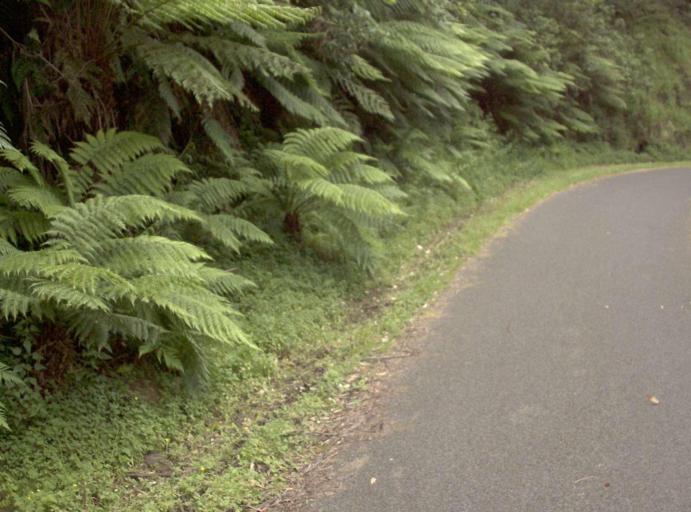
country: AU
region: Victoria
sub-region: Latrobe
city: Traralgon
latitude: -38.4597
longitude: 146.5478
